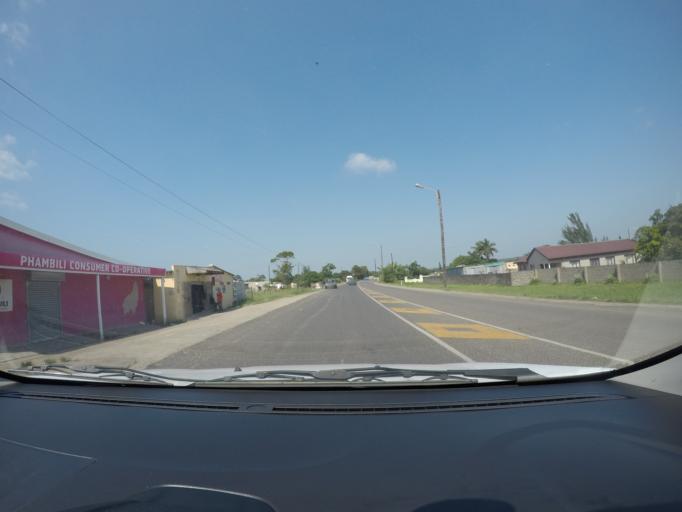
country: ZA
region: KwaZulu-Natal
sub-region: uThungulu District Municipality
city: eSikhawini
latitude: -28.8922
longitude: 31.8896
